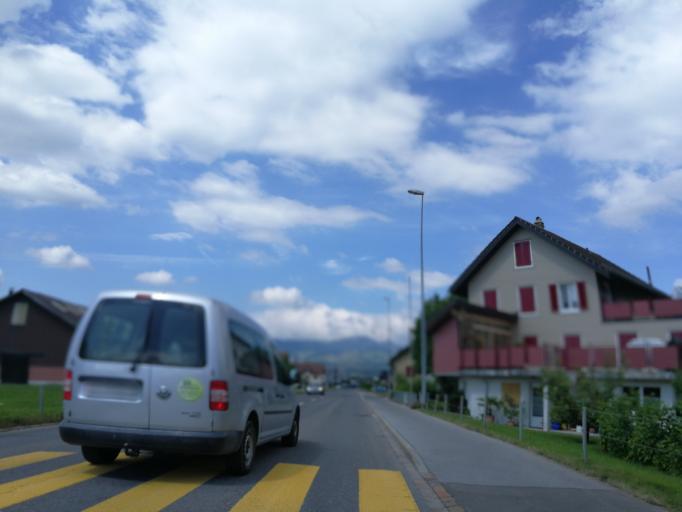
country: CH
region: Saint Gallen
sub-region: Wahlkreis See-Gaster
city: Benken
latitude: 47.1848
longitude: 8.9943
